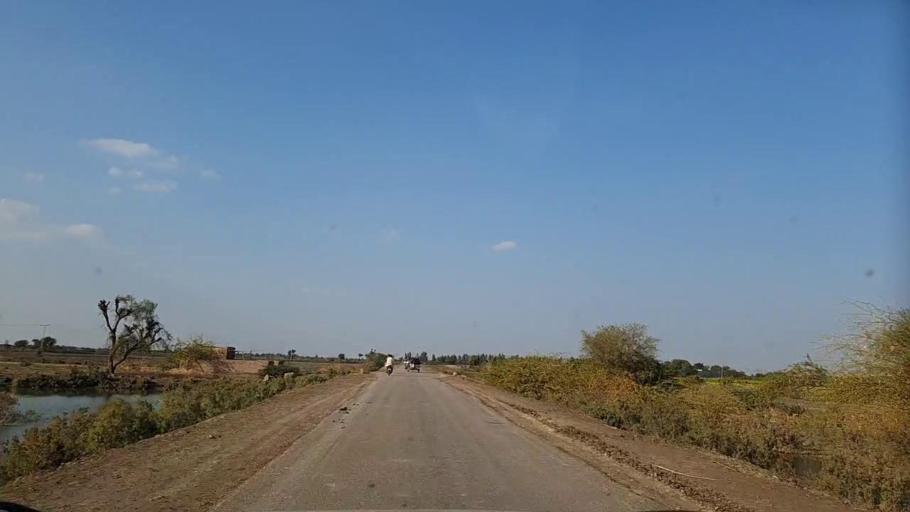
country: PK
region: Sindh
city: Pithoro
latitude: 25.7099
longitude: 69.2210
